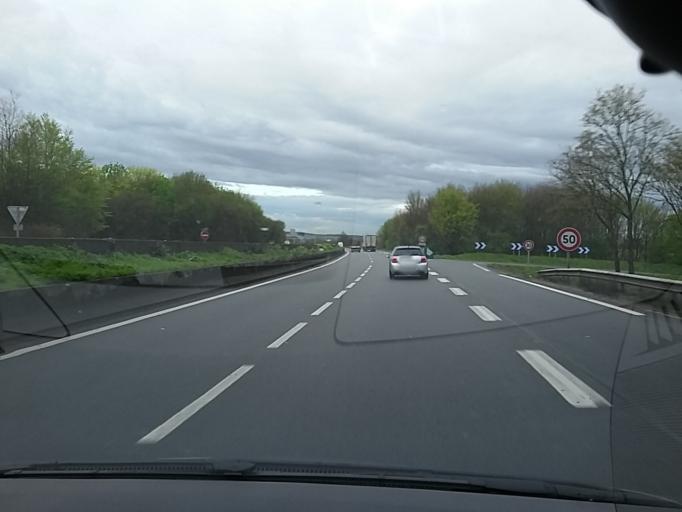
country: FR
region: Picardie
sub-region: Departement de la Somme
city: Poulainville
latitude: 49.9270
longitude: 2.3055
